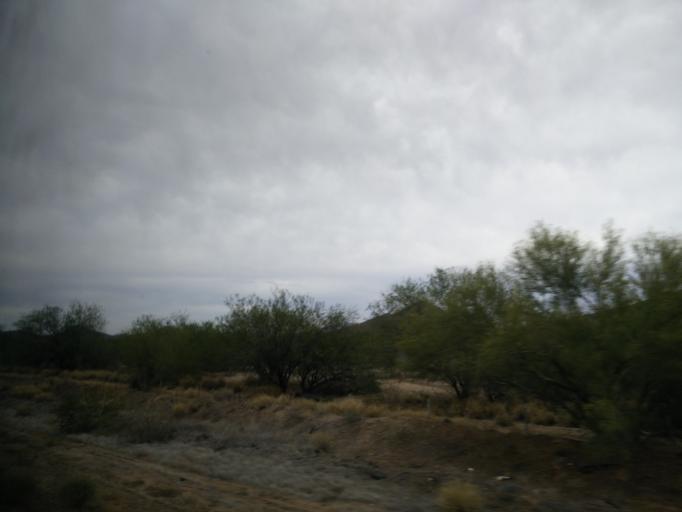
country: MX
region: Sonora
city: Hermosillo
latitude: 28.8213
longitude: -110.9580
